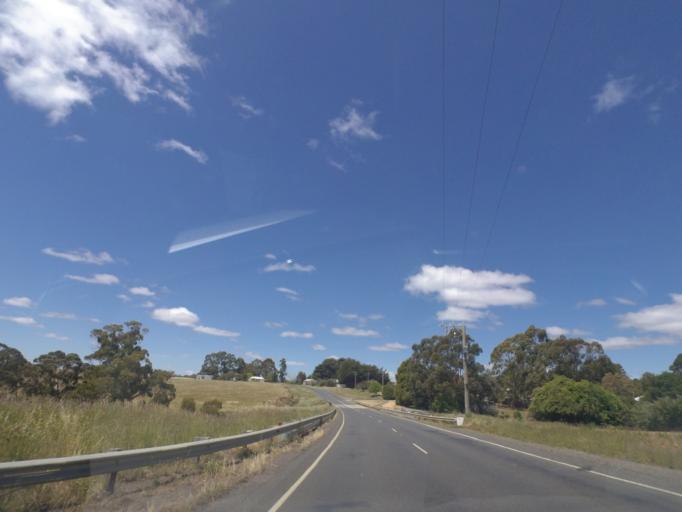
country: AU
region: Victoria
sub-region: Mount Alexander
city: Castlemaine
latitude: -37.3307
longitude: 144.1837
